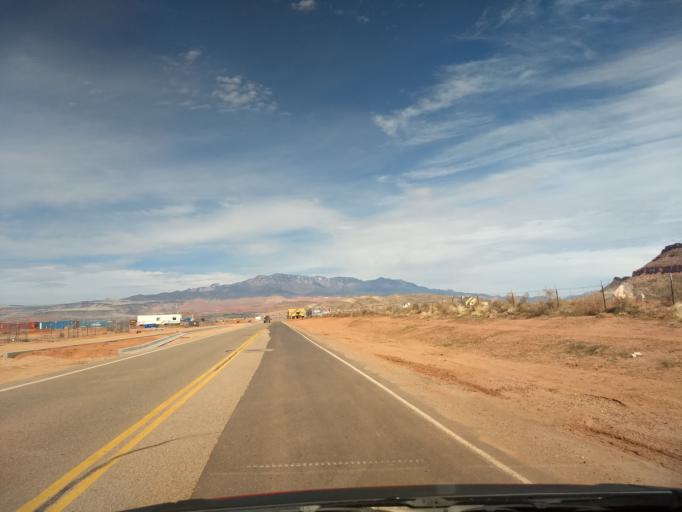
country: US
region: Utah
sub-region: Washington County
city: Washington
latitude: 37.0602
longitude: -113.4902
